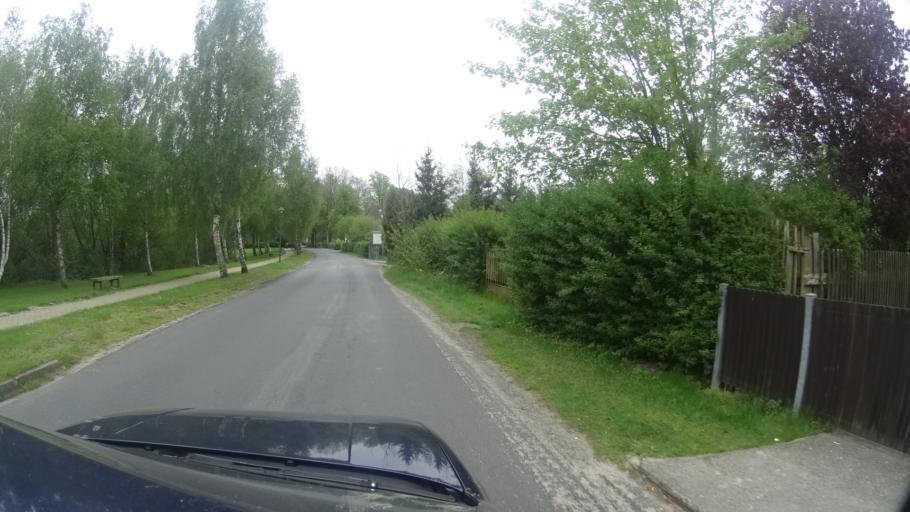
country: DE
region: Mecklenburg-Vorpommern
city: Ribnitz-Damgarten
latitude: 54.2420
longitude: 12.4277
